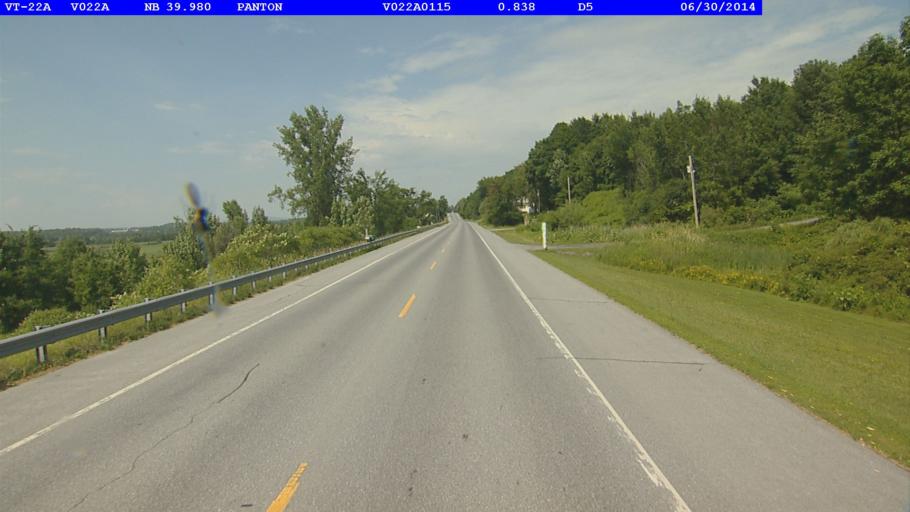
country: US
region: Vermont
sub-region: Addison County
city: Vergennes
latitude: 44.1308
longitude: -73.2873
